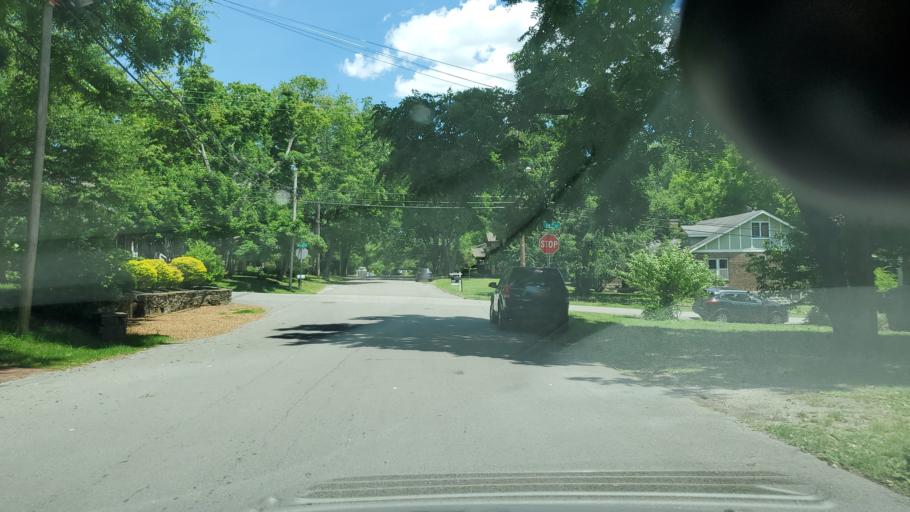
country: US
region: Tennessee
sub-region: Davidson County
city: Nashville
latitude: 36.1912
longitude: -86.7421
